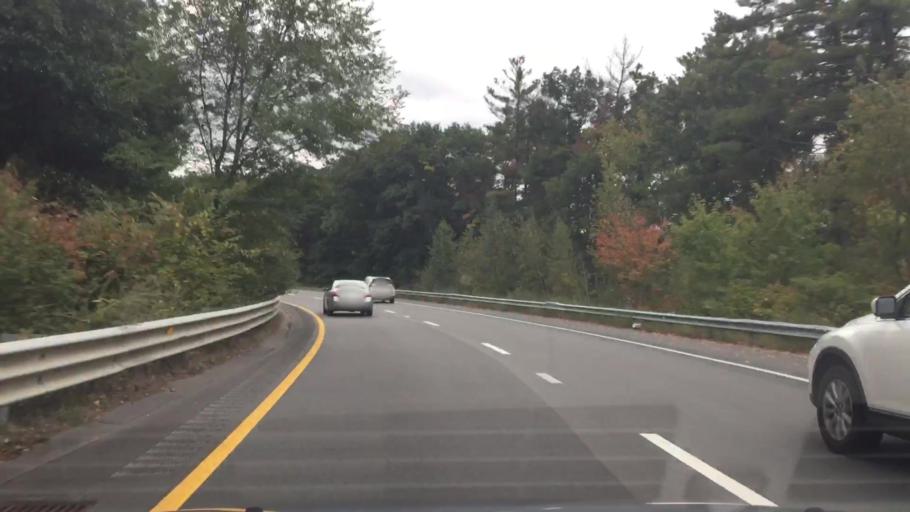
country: US
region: Massachusetts
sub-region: Middlesex County
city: Lowell
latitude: 42.6050
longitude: -71.3207
